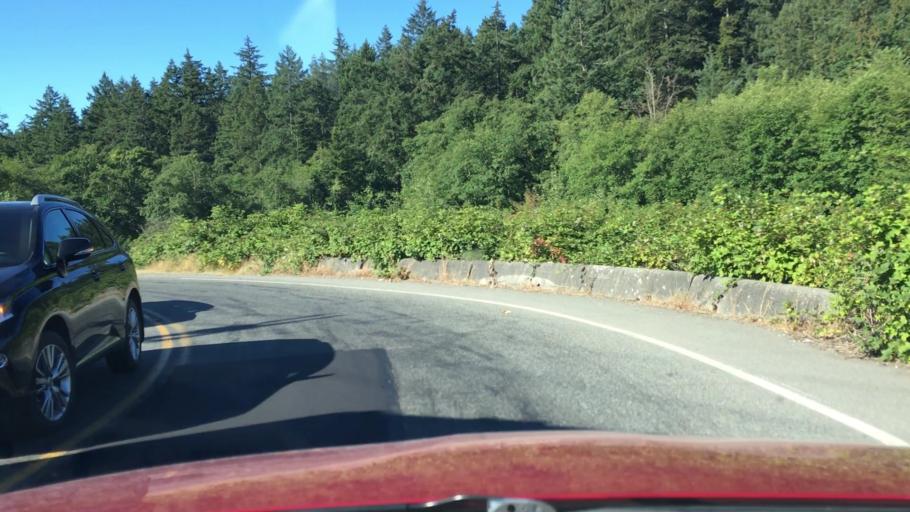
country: CA
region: British Columbia
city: Victoria
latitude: 48.5142
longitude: -123.3848
